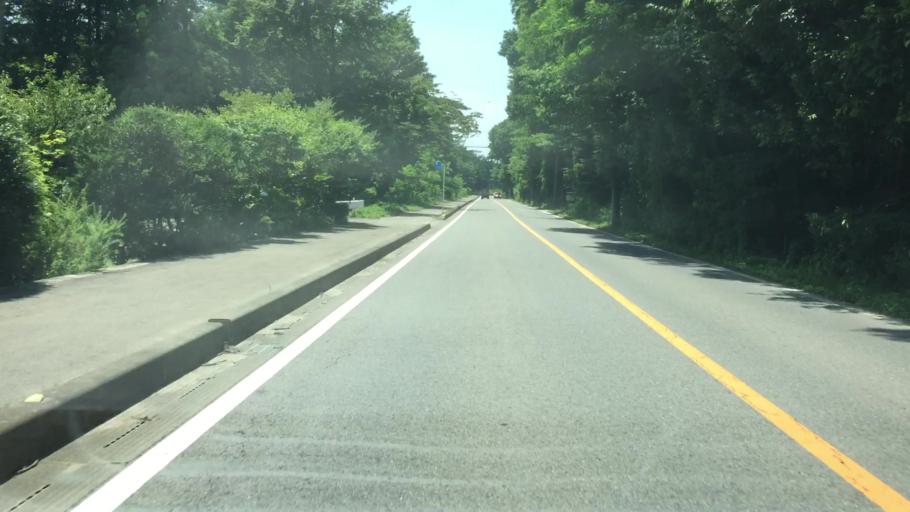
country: JP
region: Tochigi
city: Kuroiso
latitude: 37.0170
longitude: 139.9667
